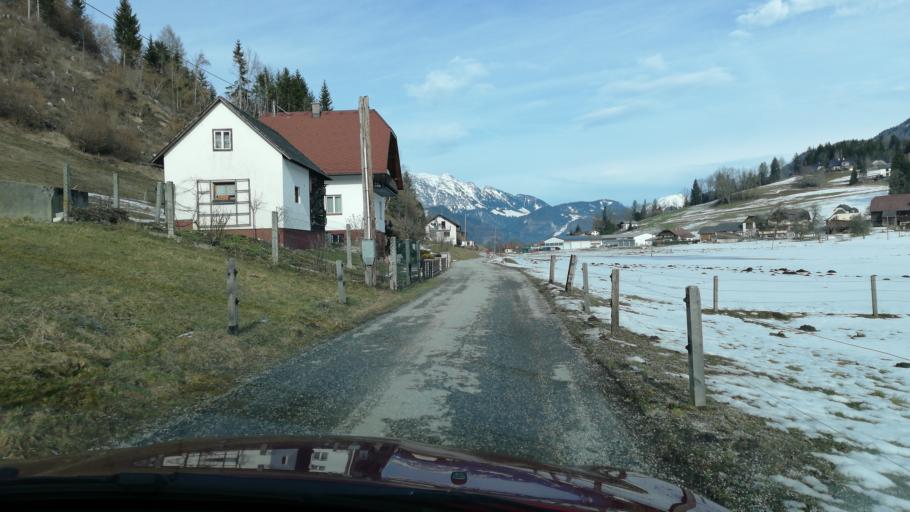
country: AT
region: Styria
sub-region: Politischer Bezirk Liezen
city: Aigen im Ennstal
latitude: 47.5221
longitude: 14.1328
